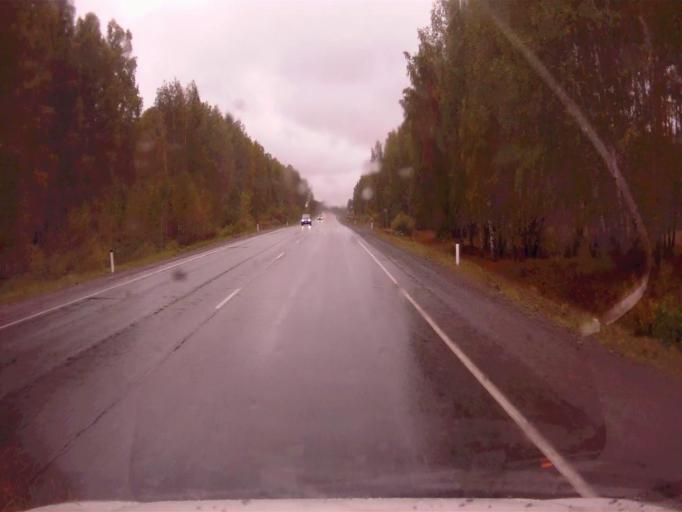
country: RU
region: Chelyabinsk
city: Argayash
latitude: 55.4652
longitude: 60.9121
